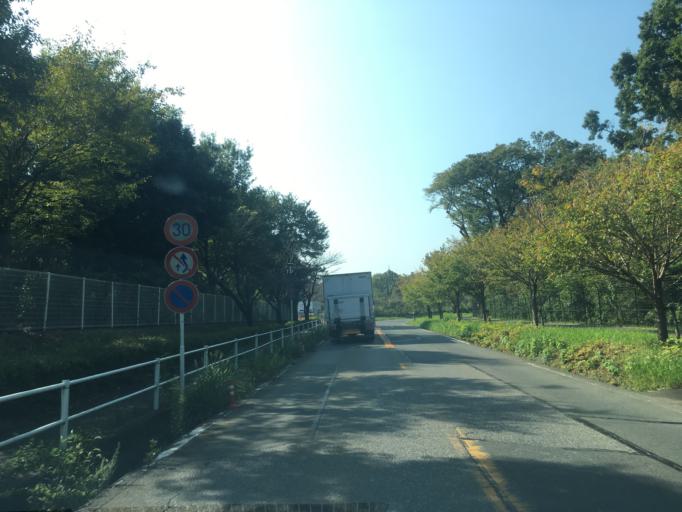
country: JP
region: Tokyo
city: Higashimurayama-shi
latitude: 35.7714
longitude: 139.4150
